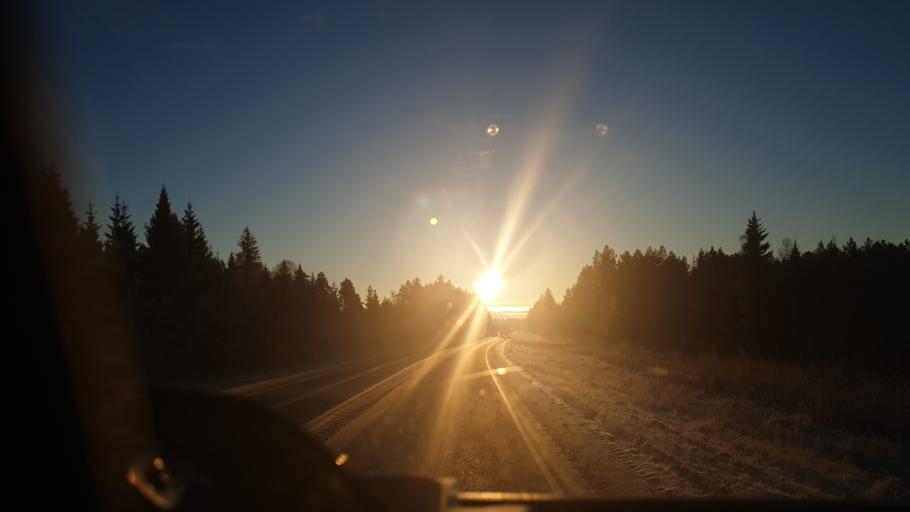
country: FI
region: Northern Ostrobothnia
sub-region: Ylivieska
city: Kalajoki
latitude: 64.2905
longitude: 23.9444
